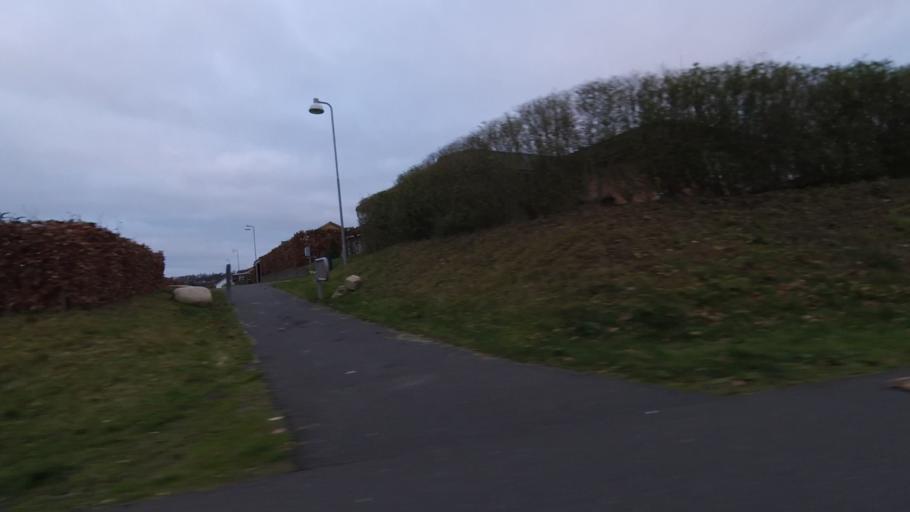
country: DK
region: Central Jutland
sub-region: Arhus Kommune
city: Stavtrup
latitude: 56.1592
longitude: 10.0919
